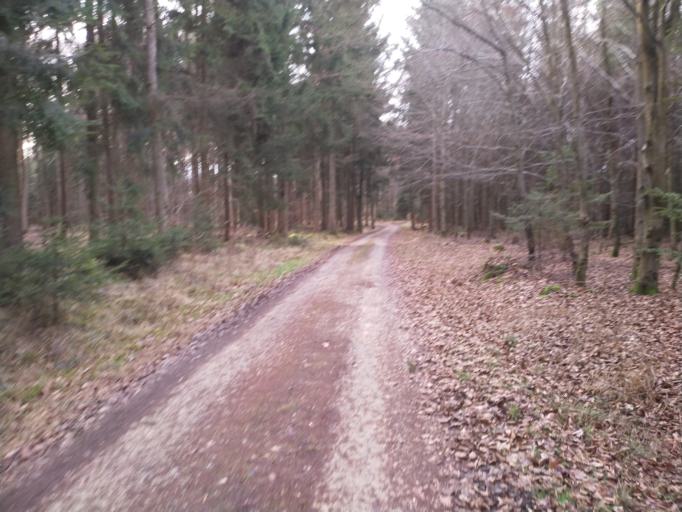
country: DE
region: Bavaria
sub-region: Swabia
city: Guenzburg
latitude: 48.4298
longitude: 10.3145
